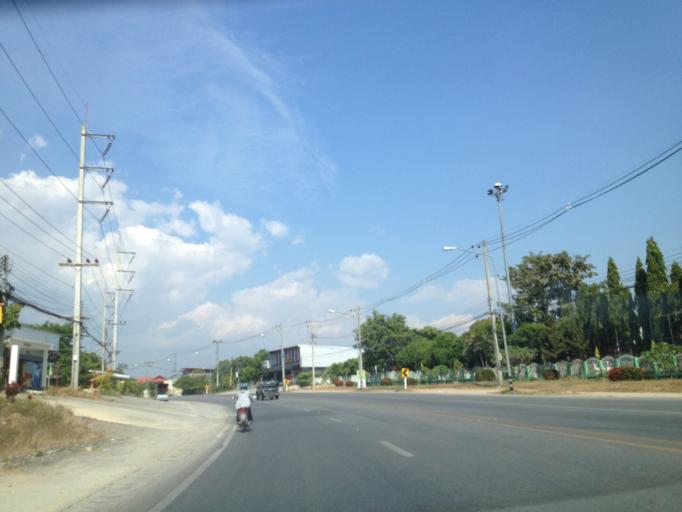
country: TH
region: Chiang Mai
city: Chom Thong
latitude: 18.3966
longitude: 98.6793
